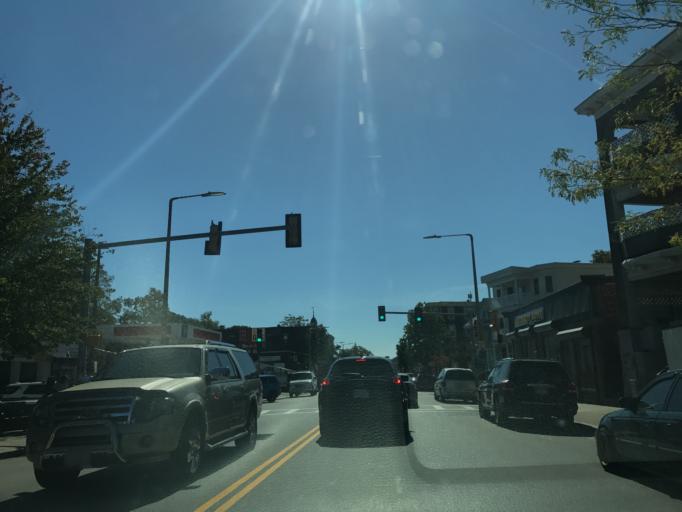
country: US
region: Massachusetts
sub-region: Norfolk County
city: Milton
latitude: 42.2938
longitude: -71.0719
